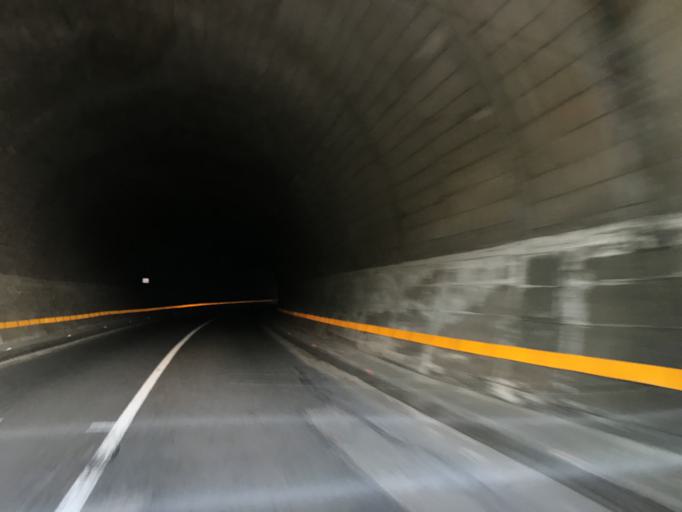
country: RO
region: Caras-Severin
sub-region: Comuna Berzasca
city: Berzasca
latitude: 44.5791
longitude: 22.0184
